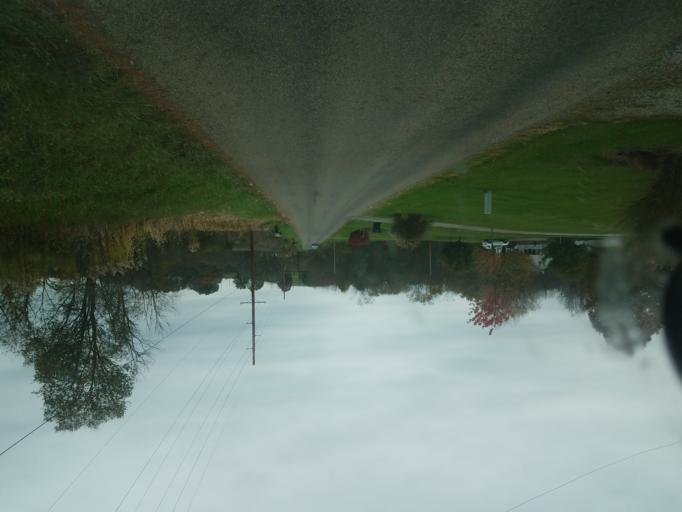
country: US
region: Ohio
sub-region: Ashland County
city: Loudonville
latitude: 40.6501
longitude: -82.2128
